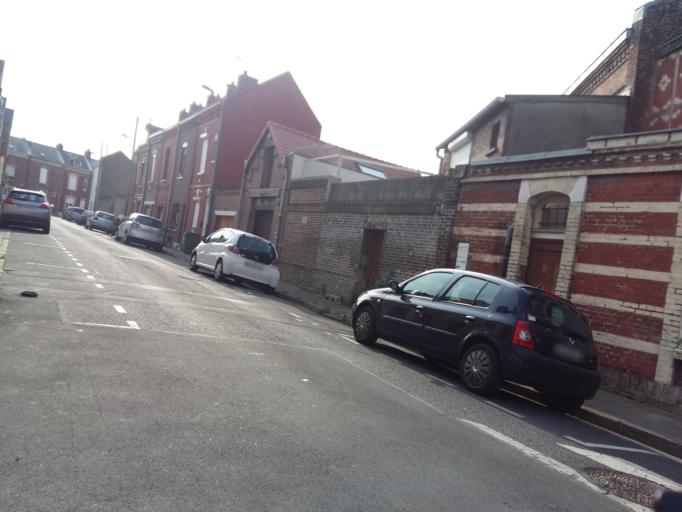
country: FR
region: Picardie
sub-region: Departement de la Somme
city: Amiens
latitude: 49.9024
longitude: 2.2965
